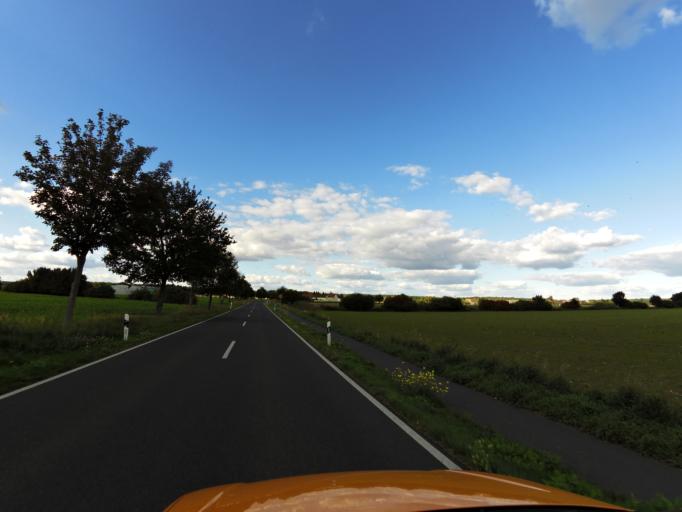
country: DE
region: Brandenburg
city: Luckenwalde
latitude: 52.1196
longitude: 13.1661
